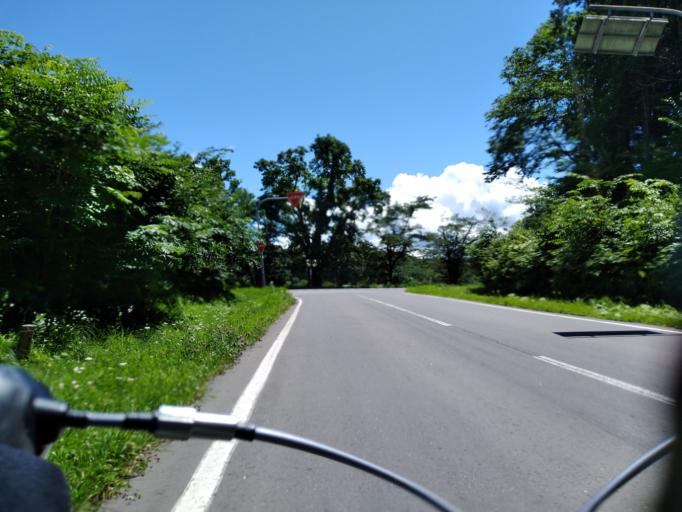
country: JP
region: Iwate
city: Shizukuishi
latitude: 39.7554
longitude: 141.0179
